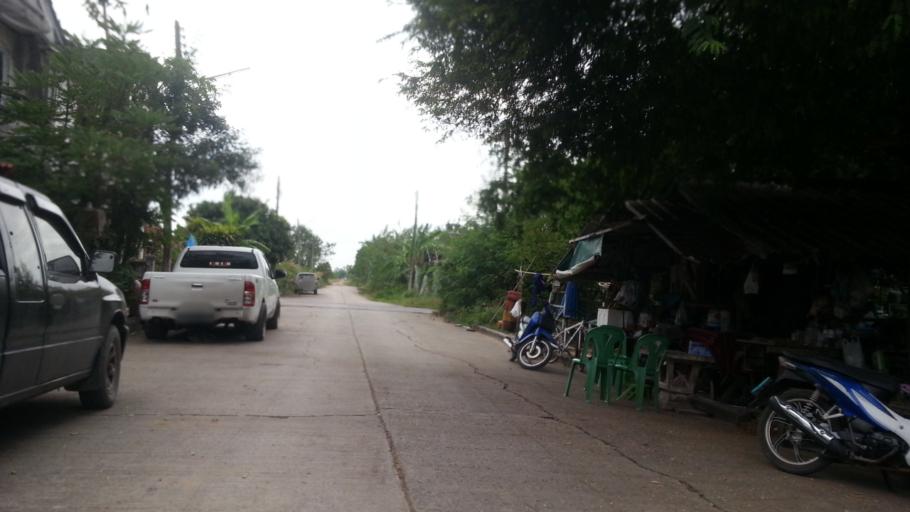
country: TH
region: Pathum Thani
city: Nong Suea
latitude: 14.0661
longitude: 100.8706
